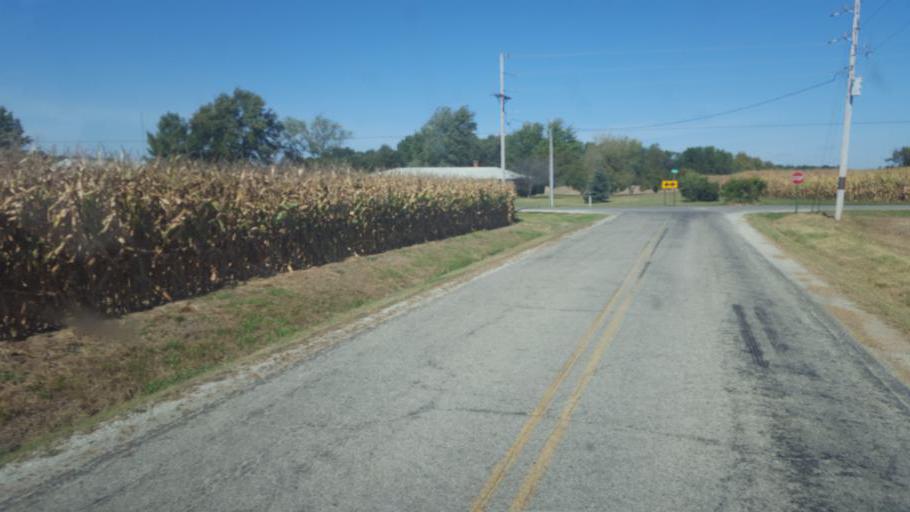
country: US
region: Ohio
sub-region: Huron County
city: Willard
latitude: 40.9814
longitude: -82.7907
